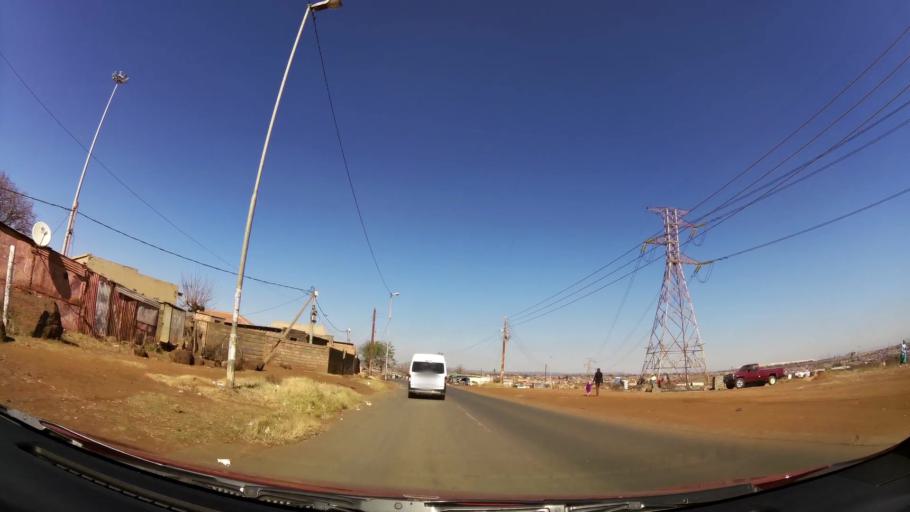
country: ZA
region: Gauteng
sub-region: City of Johannesburg Metropolitan Municipality
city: Soweto
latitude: -26.2222
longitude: 27.8198
